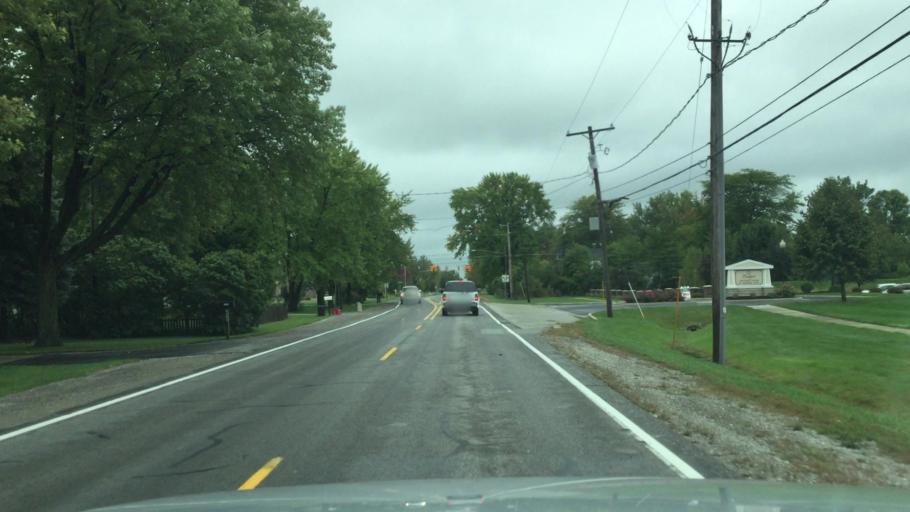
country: US
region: Michigan
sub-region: Saginaw County
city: Carrollton
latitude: 43.4739
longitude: -83.9952
